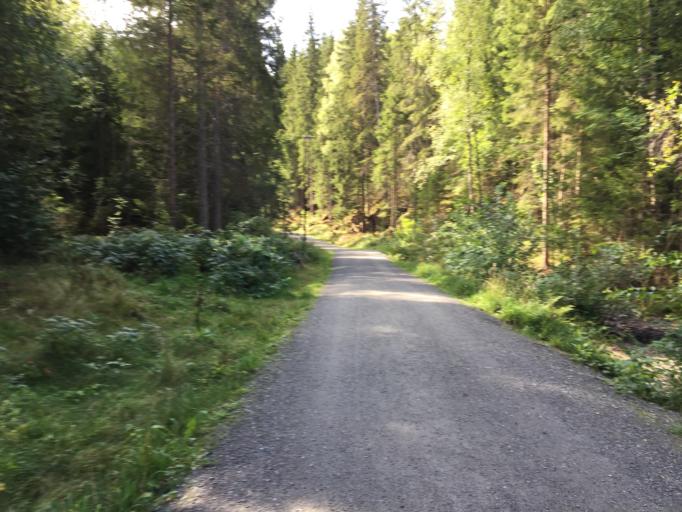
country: NO
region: Akershus
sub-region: Skedsmo
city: Lillestrom
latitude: 59.9291
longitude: 11.0291
